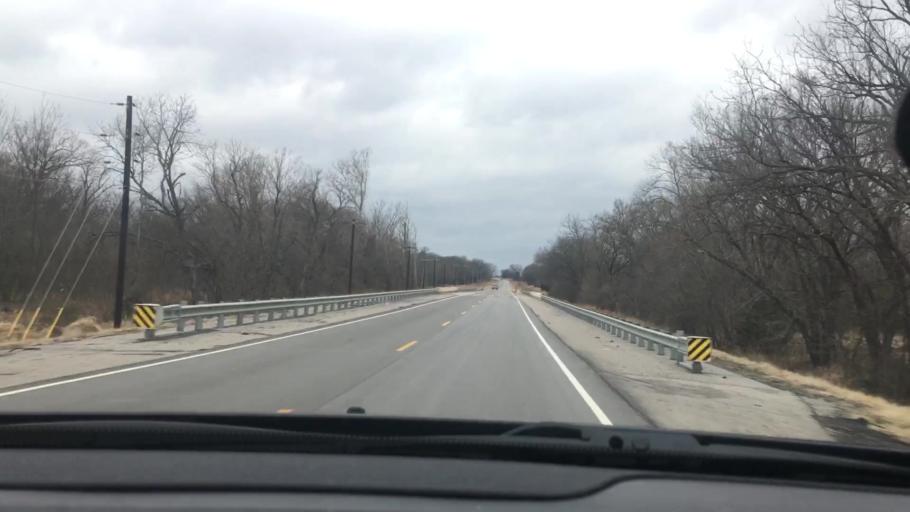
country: US
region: Oklahoma
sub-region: Atoka County
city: Atoka
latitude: 34.3791
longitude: -96.2777
